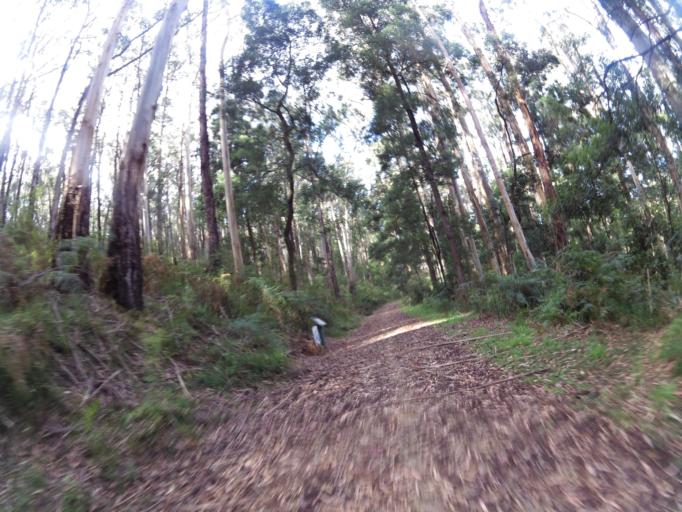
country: AU
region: Victoria
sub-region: Colac-Otway
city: Colac
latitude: -38.4907
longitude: 143.7389
